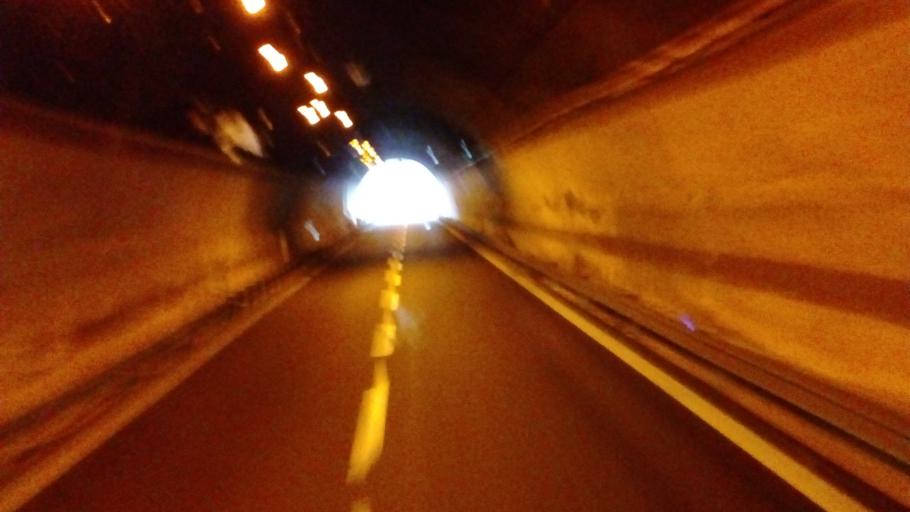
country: IT
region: Sicily
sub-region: Enna
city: Calascibetta
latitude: 37.5799
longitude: 14.2674
